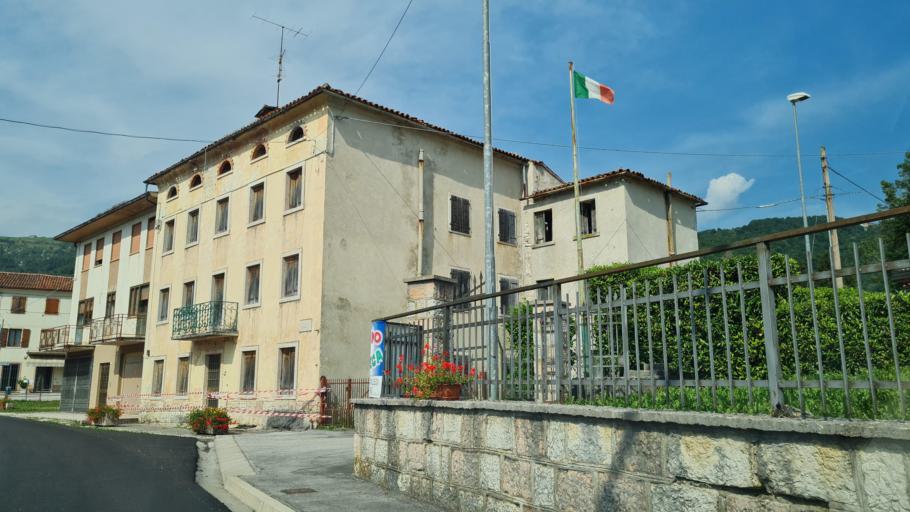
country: IT
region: Veneto
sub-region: Provincia di Vicenza
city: Conco
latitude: 45.7950
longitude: 11.6316
